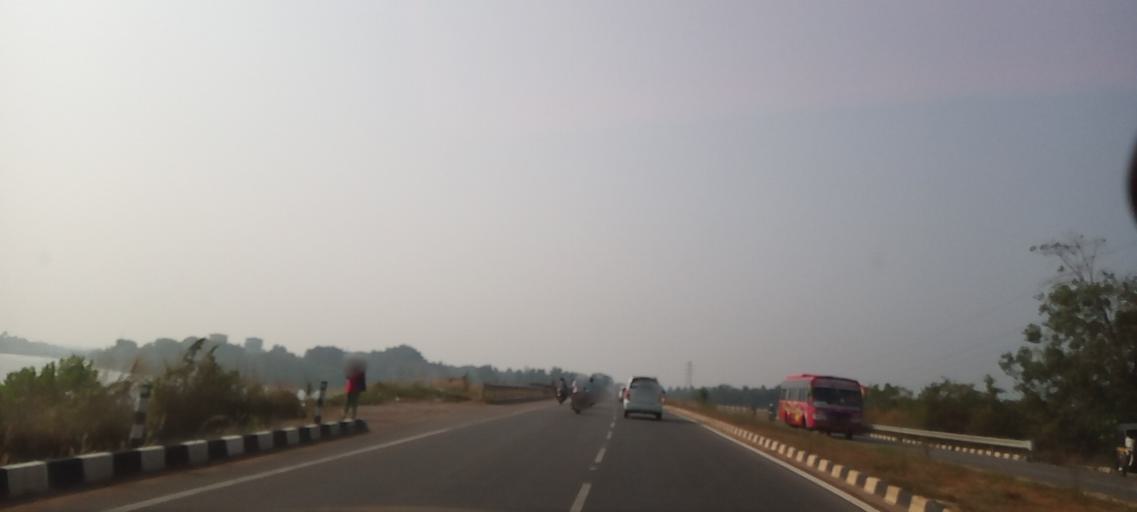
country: IN
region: Karnataka
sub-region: Udupi
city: Coondapoor
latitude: 13.6412
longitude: 74.7013
